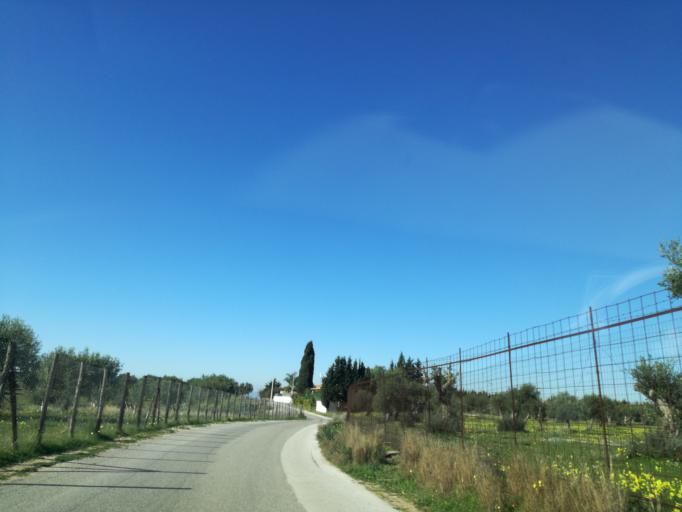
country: IT
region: Sicily
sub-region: Provincia di Caltanissetta
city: Niscemi
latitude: 37.0597
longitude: 14.3546
